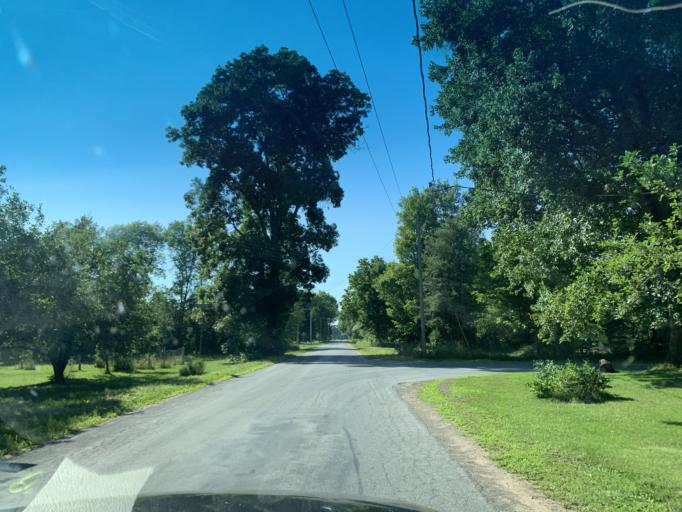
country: US
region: New York
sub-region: Madison County
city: Oneida
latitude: 43.1511
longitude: -75.6621
